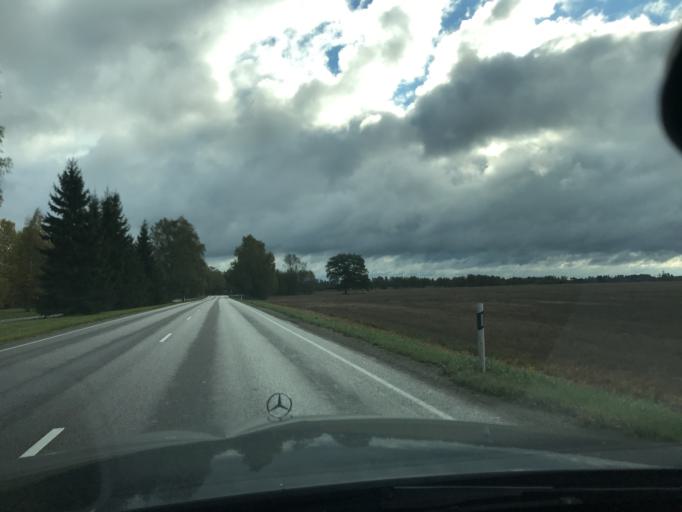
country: EE
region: Valgamaa
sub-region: Torva linn
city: Torva
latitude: 58.0302
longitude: 25.8508
